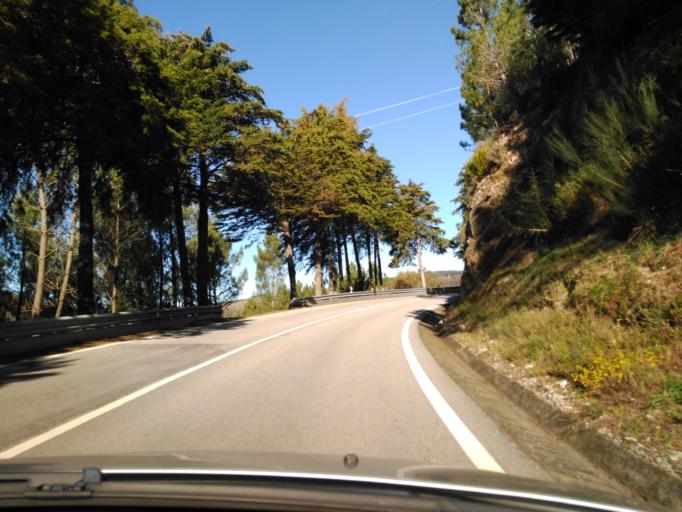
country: PT
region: Braga
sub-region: Cabeceiras de Basto
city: Cabeceiras de Basto
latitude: 41.6698
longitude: -7.9834
